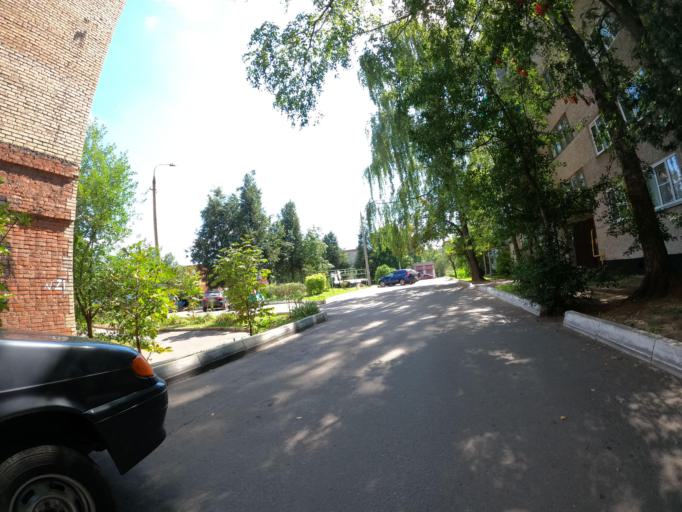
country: RU
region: Moskovskaya
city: Stupino
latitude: 54.8860
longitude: 38.0883
